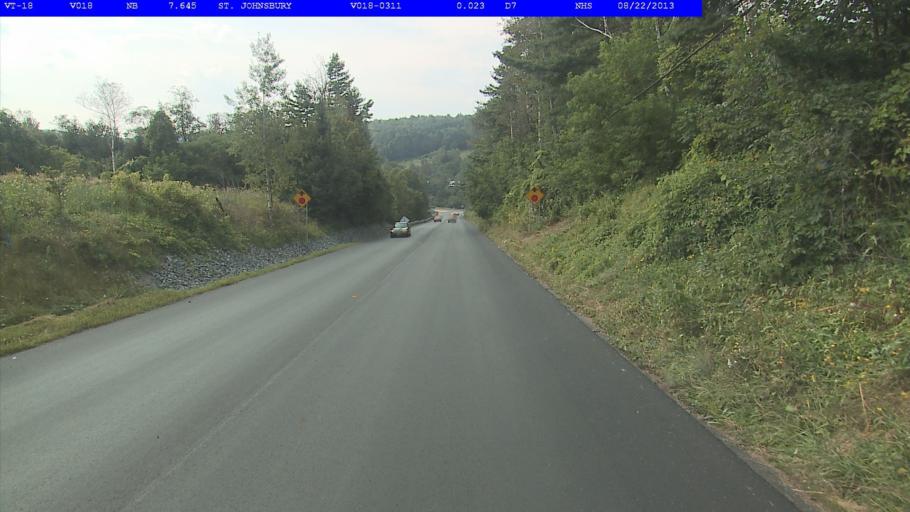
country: US
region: Vermont
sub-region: Caledonia County
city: St Johnsbury
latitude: 44.4277
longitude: -71.9597
